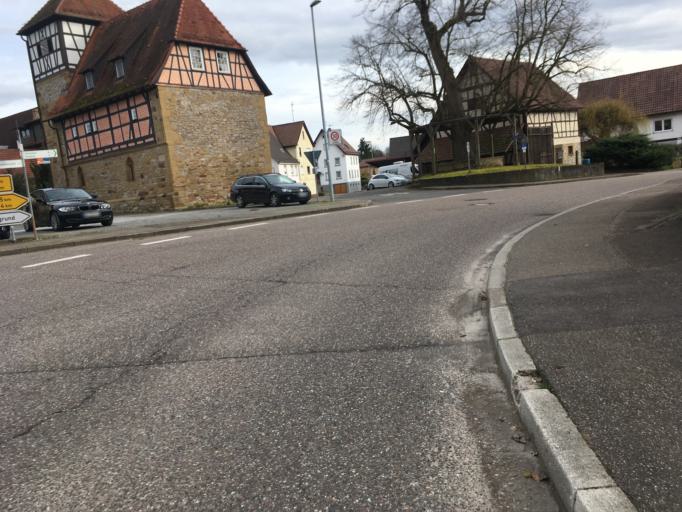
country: DE
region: Baden-Wuerttemberg
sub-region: Regierungsbezirk Stuttgart
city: Bretzfeld
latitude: 49.2160
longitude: 9.4064
